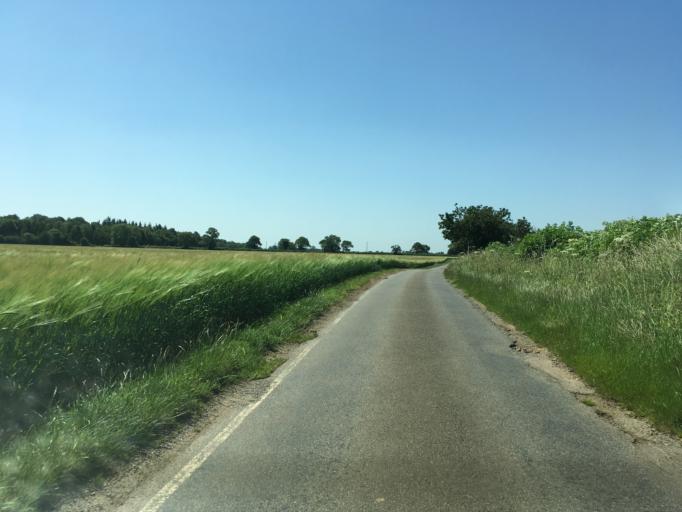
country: GB
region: England
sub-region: Northamptonshire
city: Brackley
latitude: 51.9975
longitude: -1.1047
